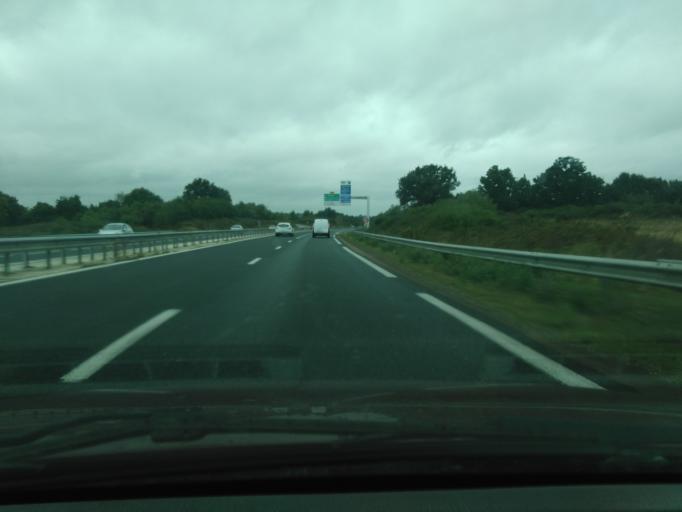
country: FR
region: Pays de la Loire
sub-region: Departement de la Vendee
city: La Ferriere
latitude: 46.6690
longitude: -1.3566
